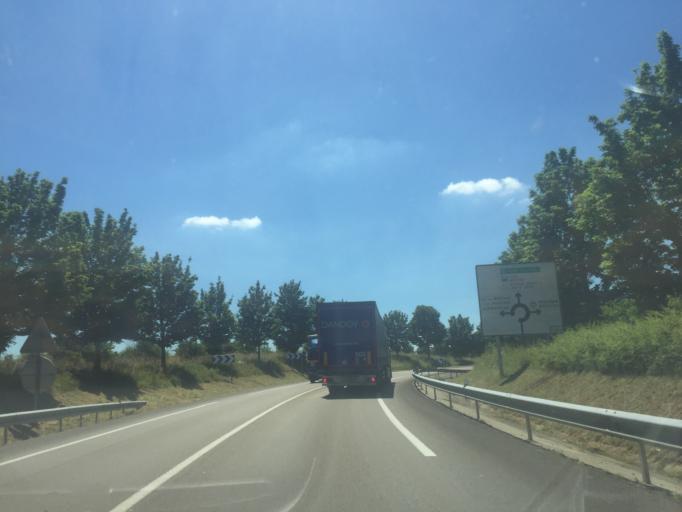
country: FR
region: Rhone-Alpes
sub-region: Departement du Rhone
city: Pusignan
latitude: 45.7549
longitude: 5.0844
